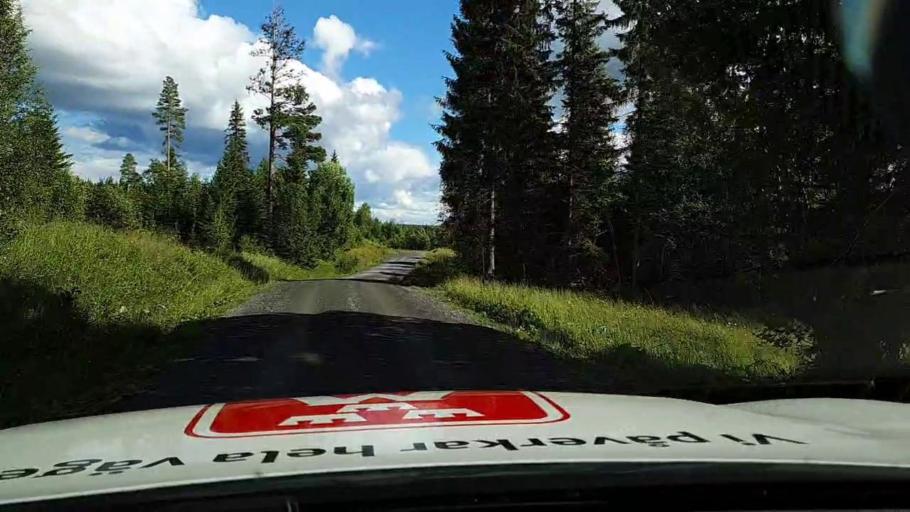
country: SE
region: Jaemtland
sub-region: Krokoms Kommun
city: Valla
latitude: 63.3275
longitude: 13.7357
